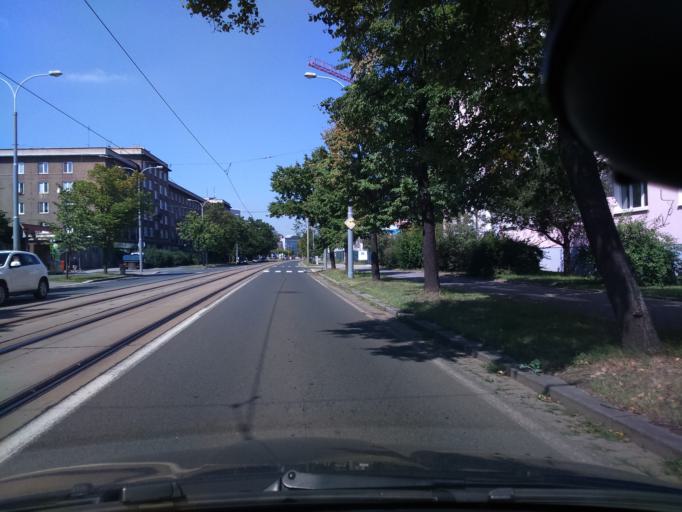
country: CZ
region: Plzensky
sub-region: Okres Plzen-Mesto
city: Pilsen
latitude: 49.7309
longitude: 13.4058
